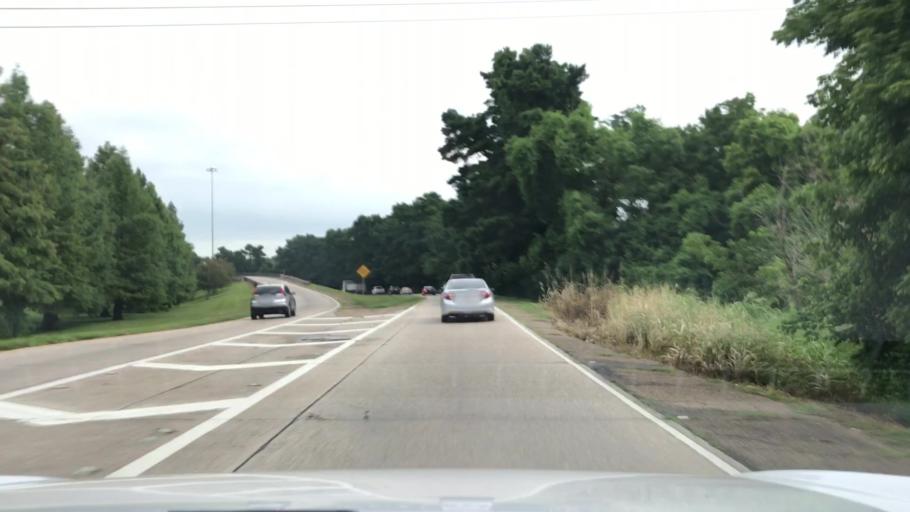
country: US
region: Louisiana
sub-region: East Baton Rouge Parish
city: Brownsfield
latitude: 30.5149
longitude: -91.1581
